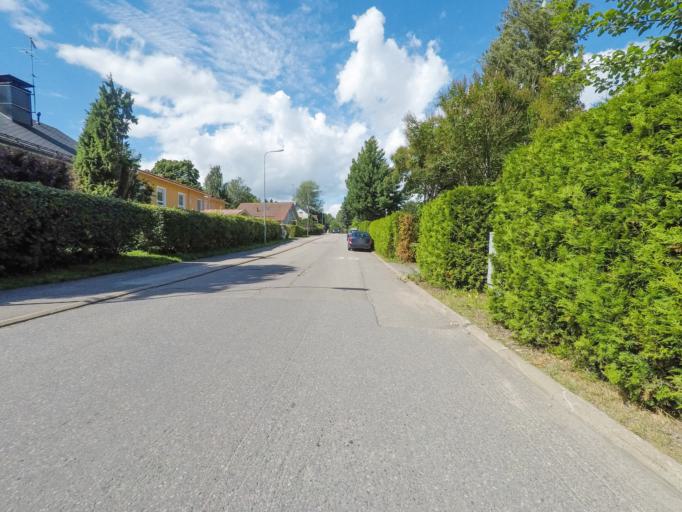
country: FI
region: Uusimaa
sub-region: Helsinki
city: Vantaa
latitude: 60.2172
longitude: 25.1127
